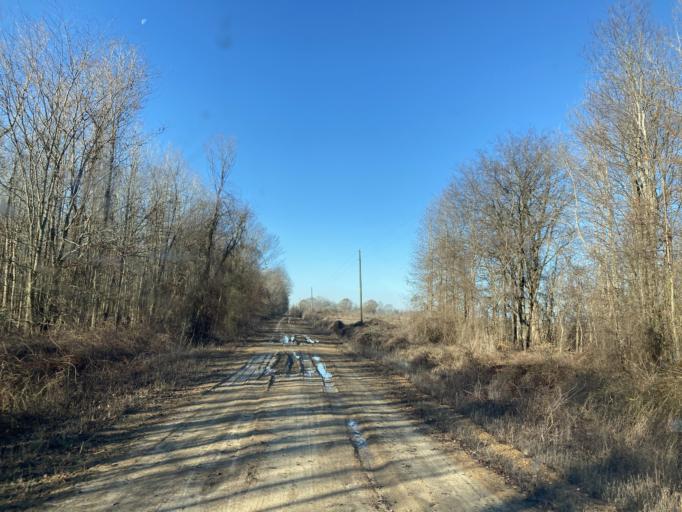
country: US
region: Mississippi
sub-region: Yazoo County
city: Yazoo City
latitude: 32.9371
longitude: -90.5593
